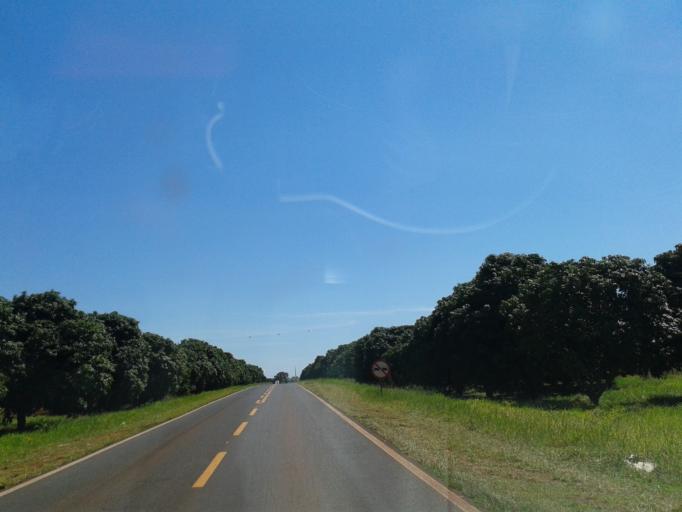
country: BR
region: Minas Gerais
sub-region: Centralina
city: Centralina
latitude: -18.7157
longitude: -49.1386
